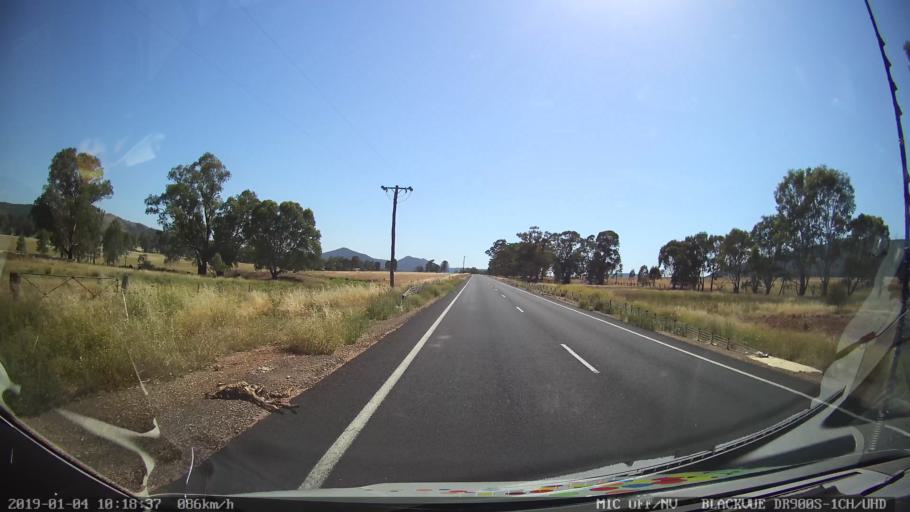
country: AU
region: New South Wales
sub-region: Cabonne
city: Canowindra
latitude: -33.3812
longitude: 148.4691
